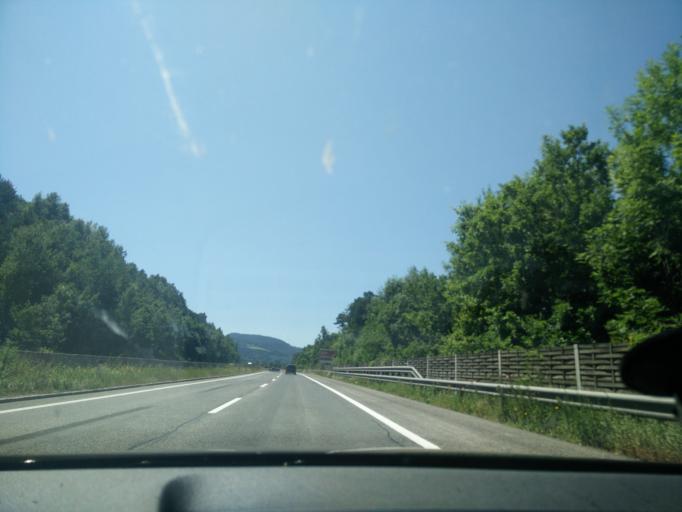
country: AT
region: Lower Austria
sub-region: Politischer Bezirk Neunkirchen
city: Grimmenstein
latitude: 47.6185
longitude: 16.1305
